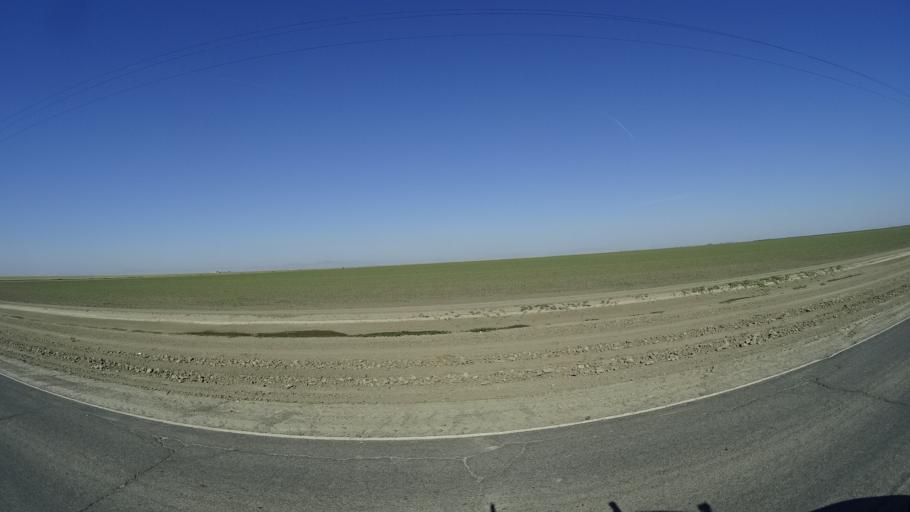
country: US
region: California
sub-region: Kings County
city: Corcoran
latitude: 36.0963
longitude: -119.6441
